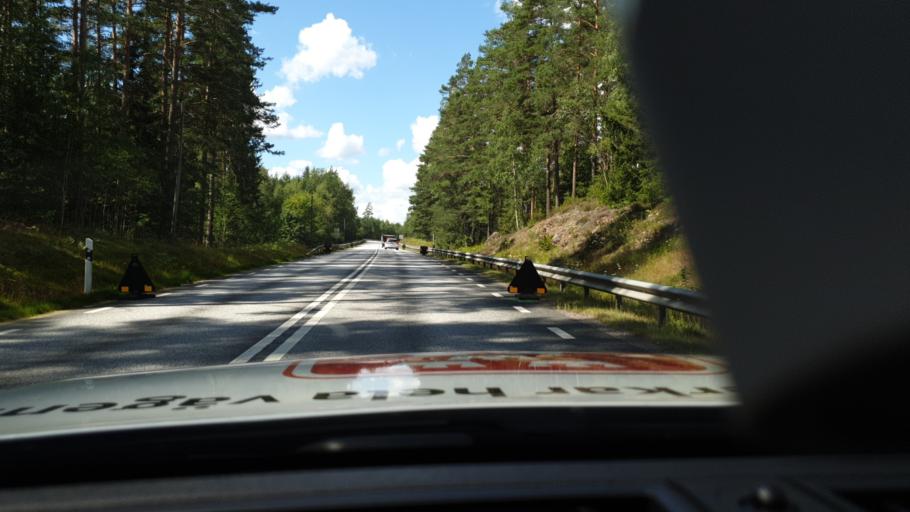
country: SE
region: Joenkoeping
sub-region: Eksjo Kommun
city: Haljarp
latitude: 57.6295
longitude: 15.4379
